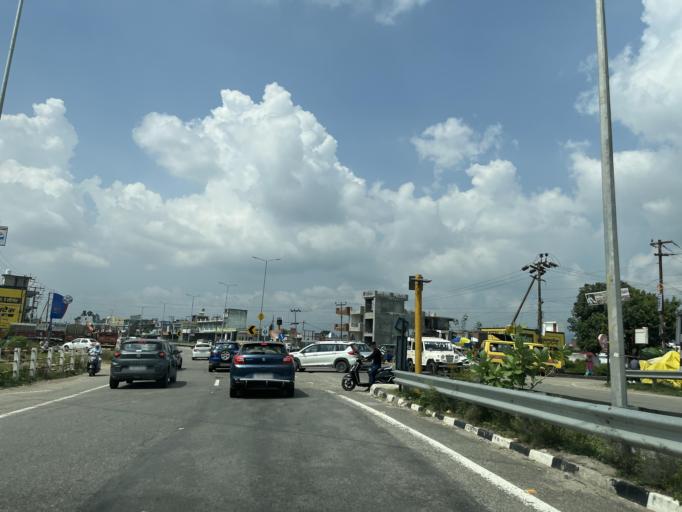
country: IN
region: Uttarakhand
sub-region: Dehradun
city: Raipur
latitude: 30.2538
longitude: 78.0938
